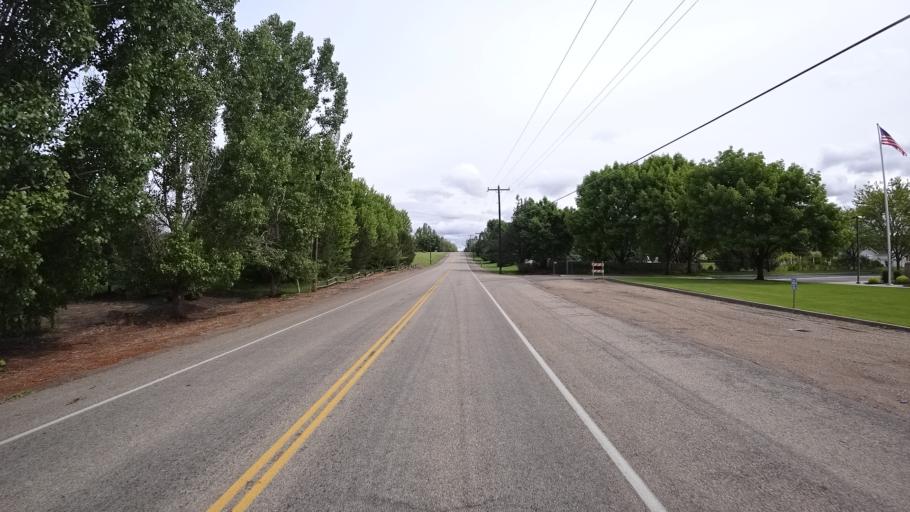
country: US
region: Idaho
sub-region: Ada County
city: Eagle
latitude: 43.7142
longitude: -116.3540
